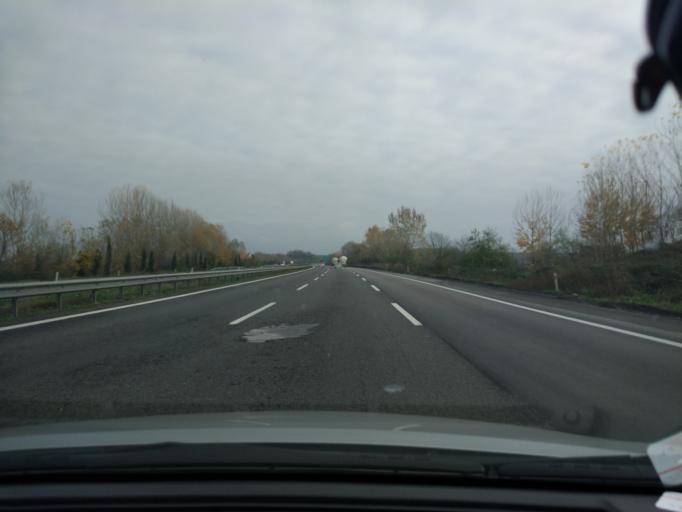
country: TR
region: Sakarya
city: Akyazi
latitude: 40.7304
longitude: 30.6364
